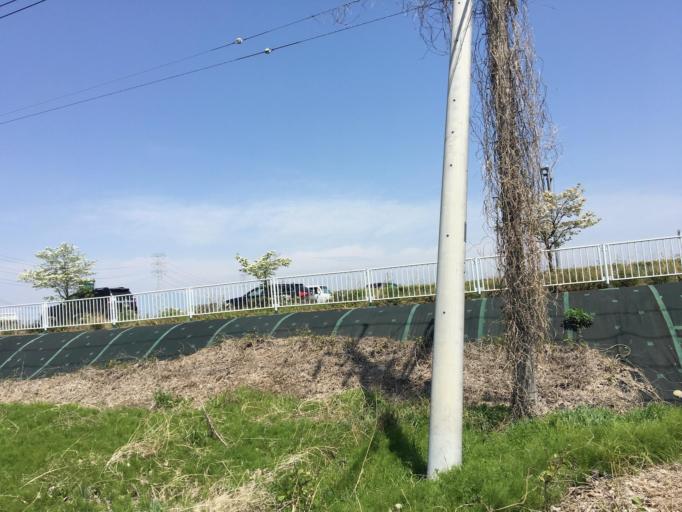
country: JP
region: Gunma
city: Sakai-nakajima
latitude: 36.2802
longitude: 139.2830
